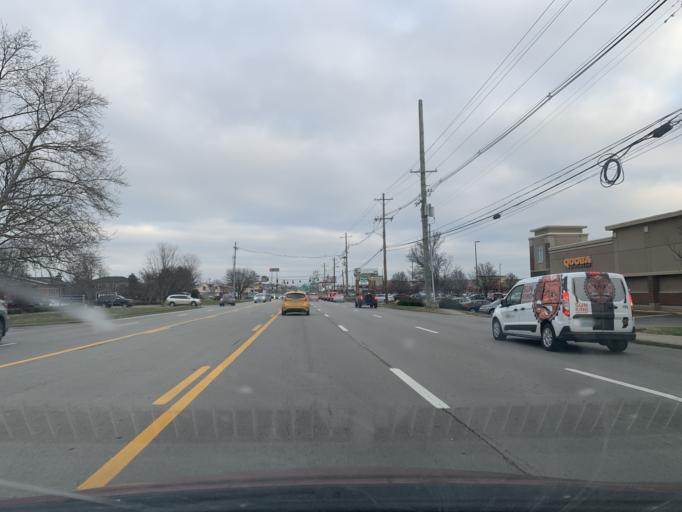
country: US
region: Kentucky
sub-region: Jefferson County
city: Beechwood Village
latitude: 38.2510
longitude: -85.6320
